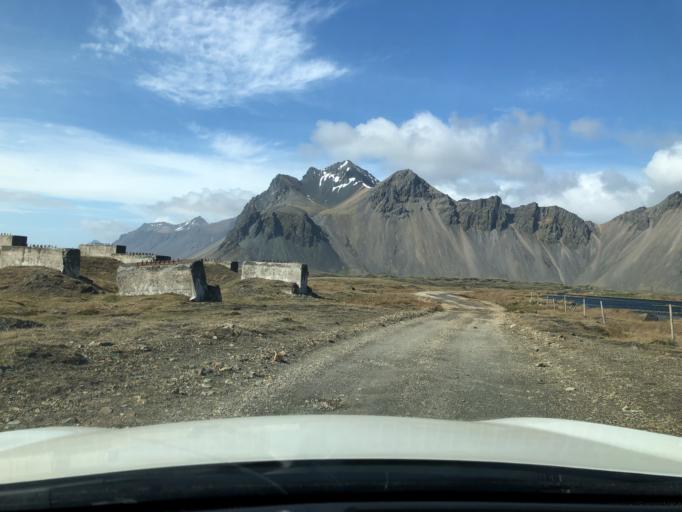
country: IS
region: East
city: Hoefn
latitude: 64.2405
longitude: -14.9714
